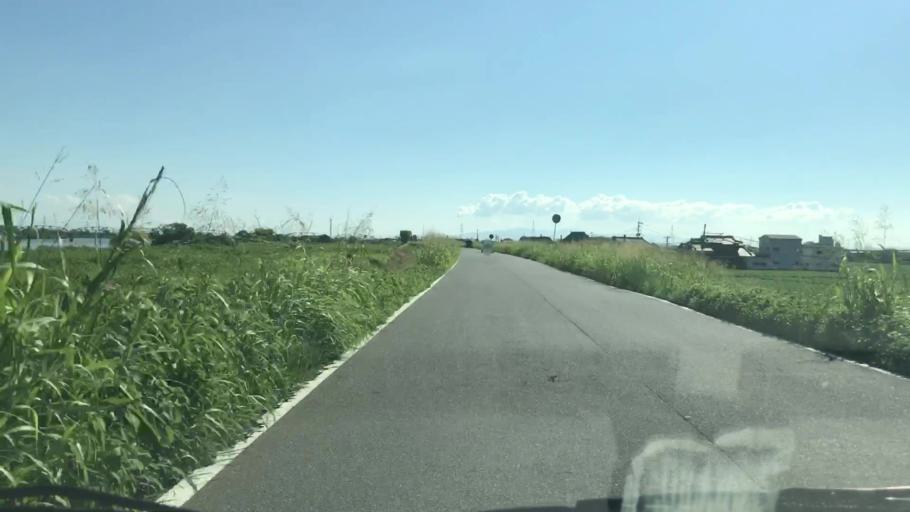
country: JP
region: Saga Prefecture
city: Kanzakimachi-kanzaki
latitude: 33.2684
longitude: 130.4224
